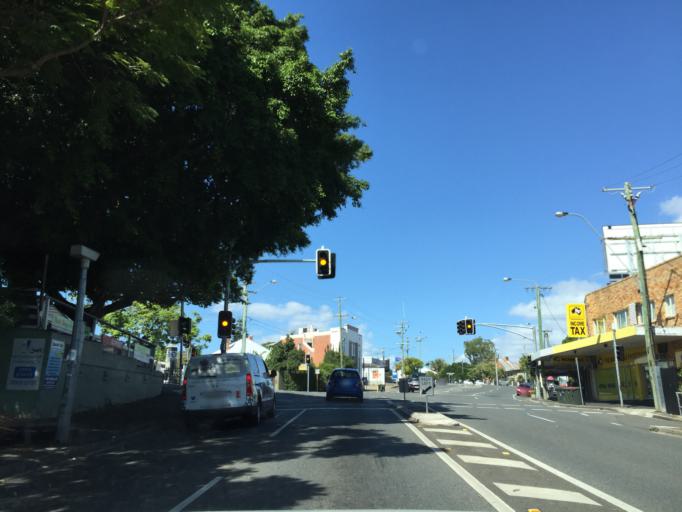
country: AU
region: Queensland
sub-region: Brisbane
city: Milton
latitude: -27.4543
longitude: 153.0065
